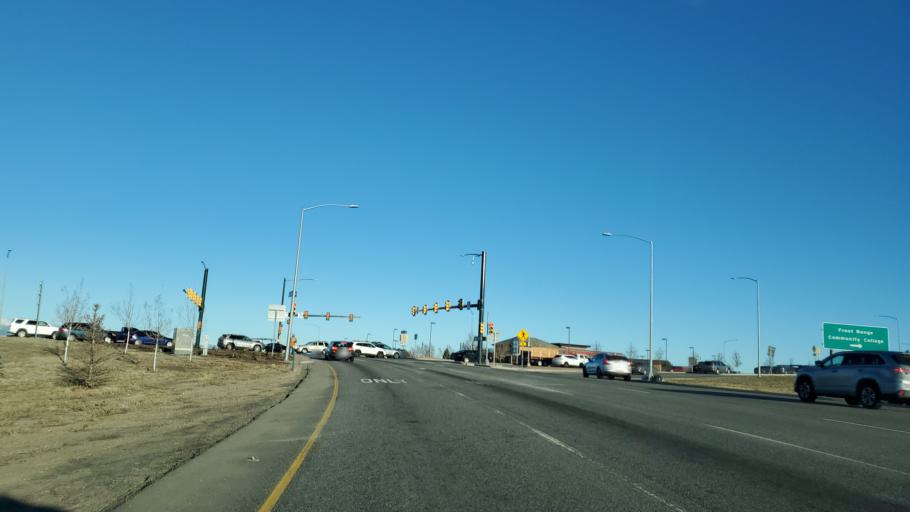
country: US
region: Colorado
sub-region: Adams County
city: Westminster
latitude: 39.8598
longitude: -105.0538
